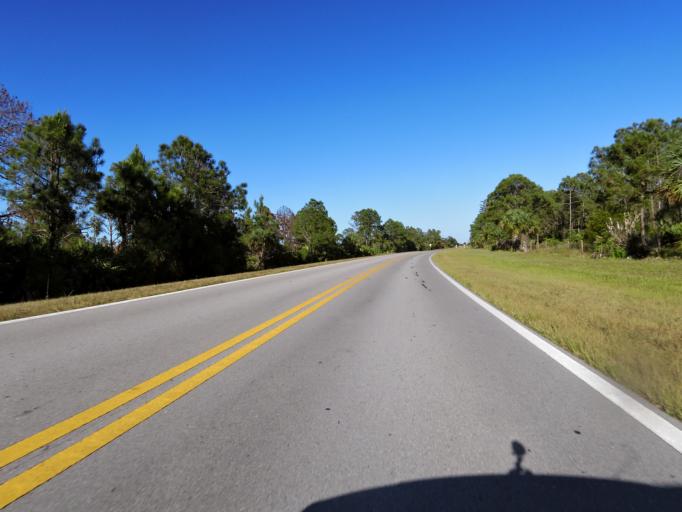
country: US
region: Florida
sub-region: Collier County
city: Immokalee
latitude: 26.3030
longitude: -81.3525
